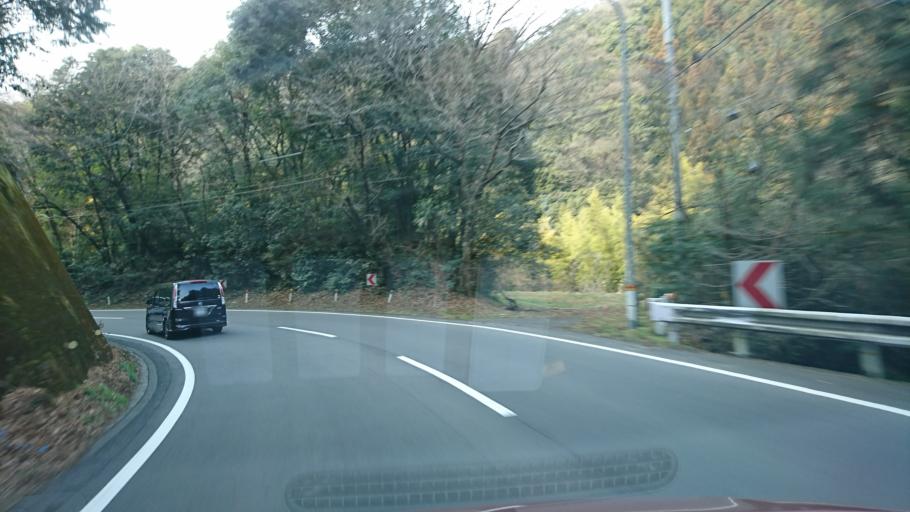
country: JP
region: Ehime
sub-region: Shikoku-chuo Shi
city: Matsuyama
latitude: 33.8981
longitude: 132.8565
